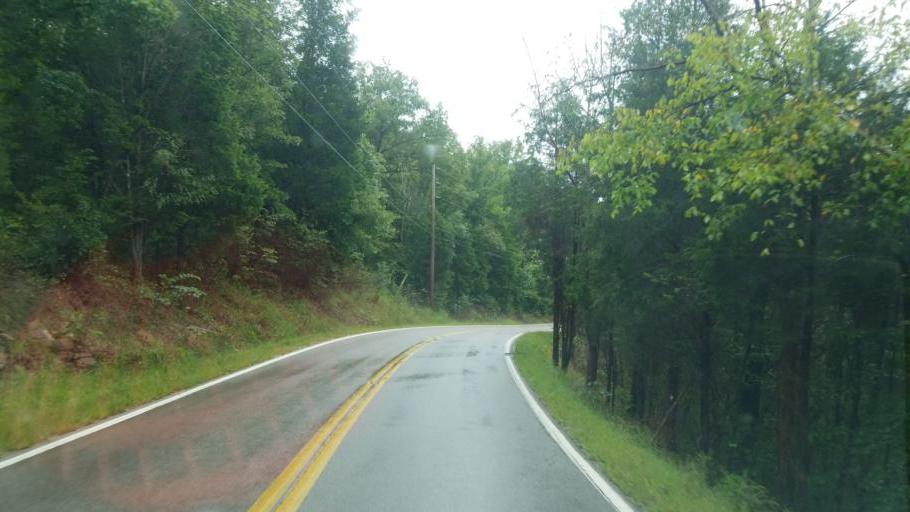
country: US
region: Ohio
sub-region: Adams County
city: West Union
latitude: 38.7712
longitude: -83.5313
